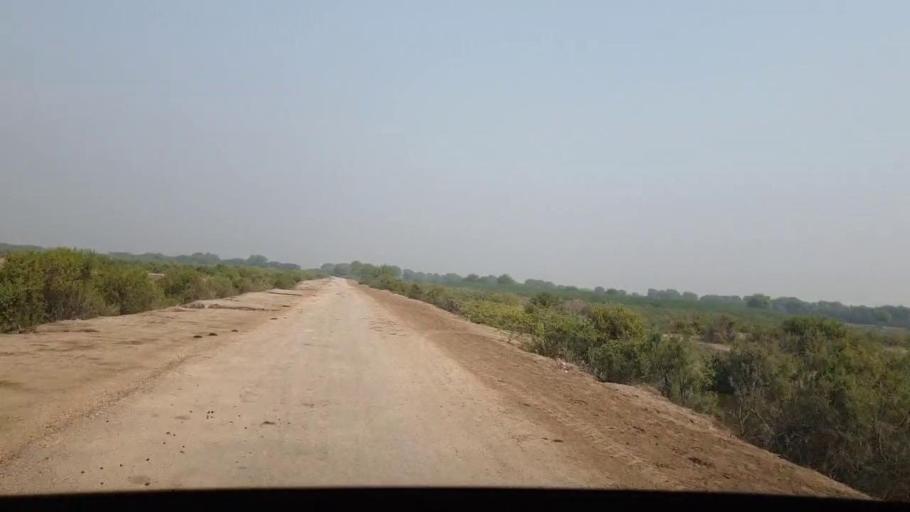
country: PK
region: Sindh
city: Jati
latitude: 24.4303
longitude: 68.4325
